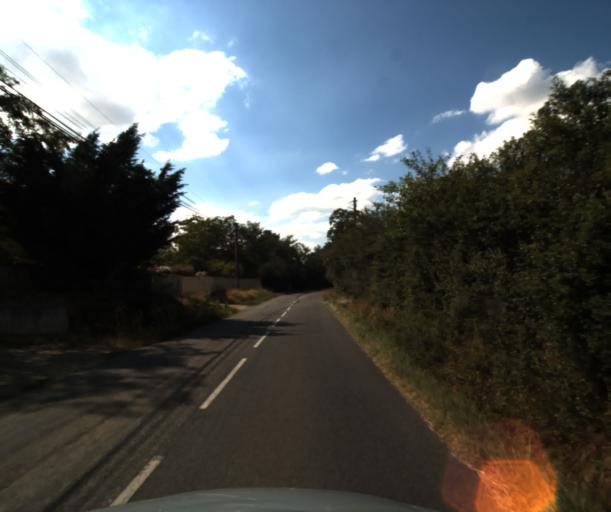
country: FR
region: Midi-Pyrenees
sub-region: Departement de la Haute-Garonne
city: Saint-Lys
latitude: 43.5209
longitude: 1.1647
